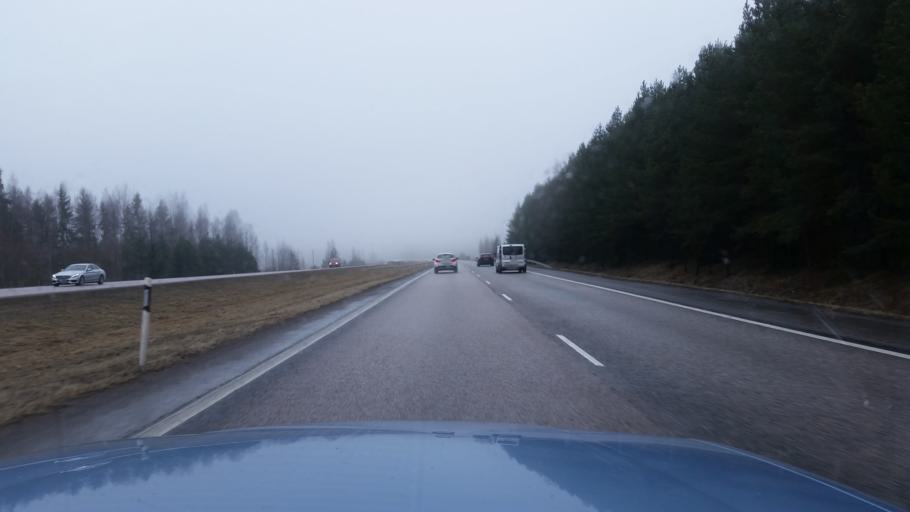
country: FI
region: Uusimaa
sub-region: Helsinki
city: Nurmijaervi
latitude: 60.4864
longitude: 24.8501
